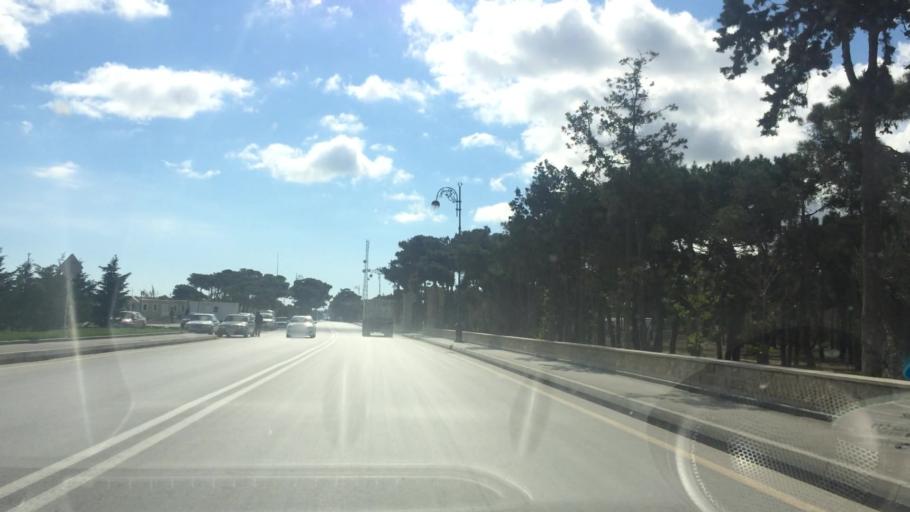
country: AZ
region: Baki
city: Pirallahi
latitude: 40.4673
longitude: 50.3268
